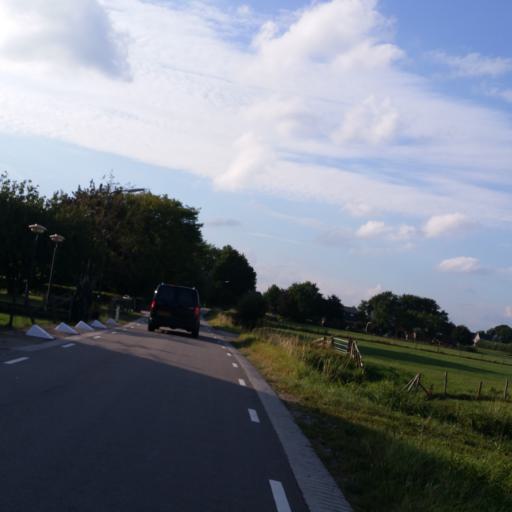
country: NL
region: Utrecht
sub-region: Gemeente Montfoort
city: Montfoort
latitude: 52.0488
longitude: 4.9952
